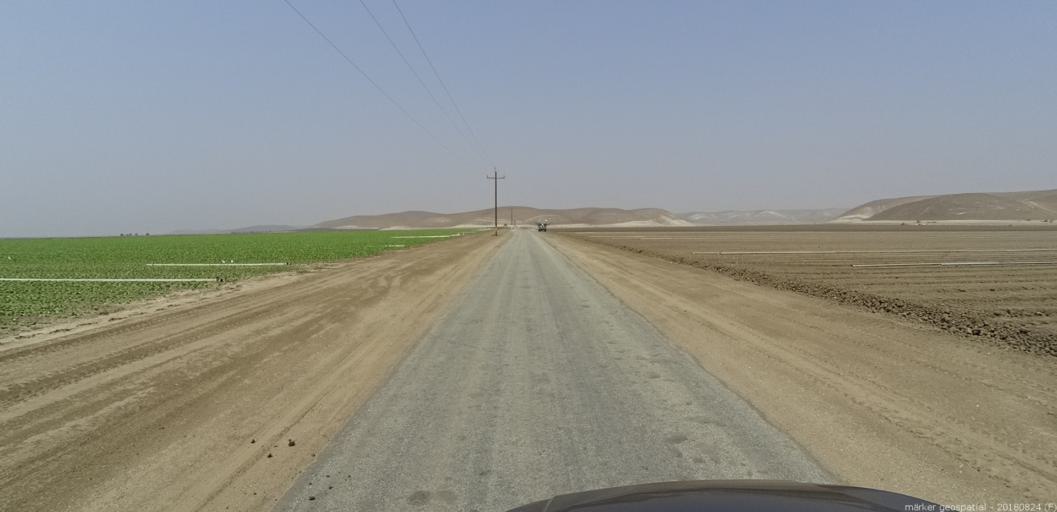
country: US
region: California
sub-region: Monterey County
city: King City
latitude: 36.1785
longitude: -121.0463
